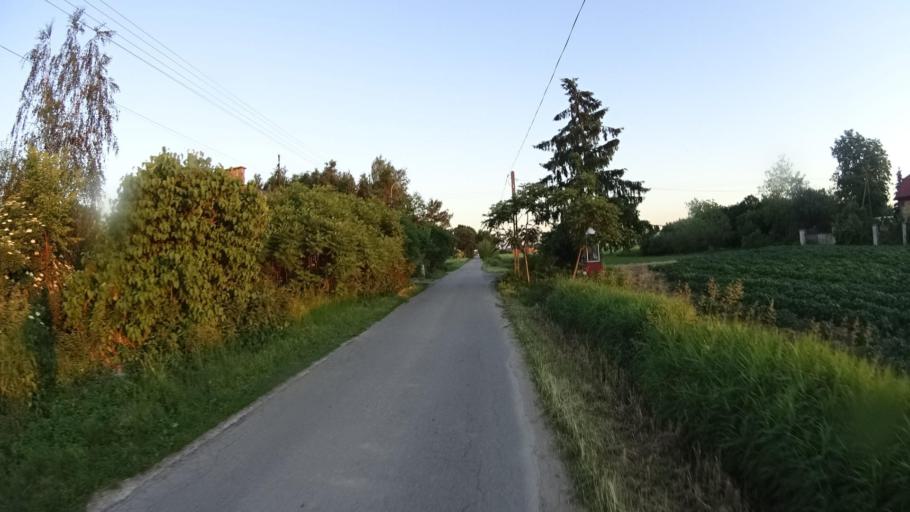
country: PL
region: Masovian Voivodeship
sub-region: Powiat warszawski zachodni
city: Blonie
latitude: 52.2406
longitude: 20.6586
